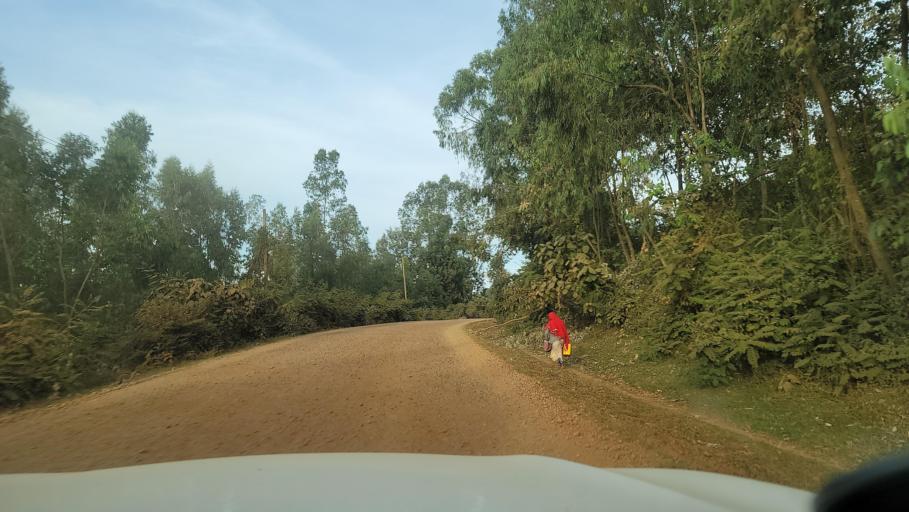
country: ET
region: Oromiya
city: Agaro
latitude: 7.8419
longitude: 36.5600
